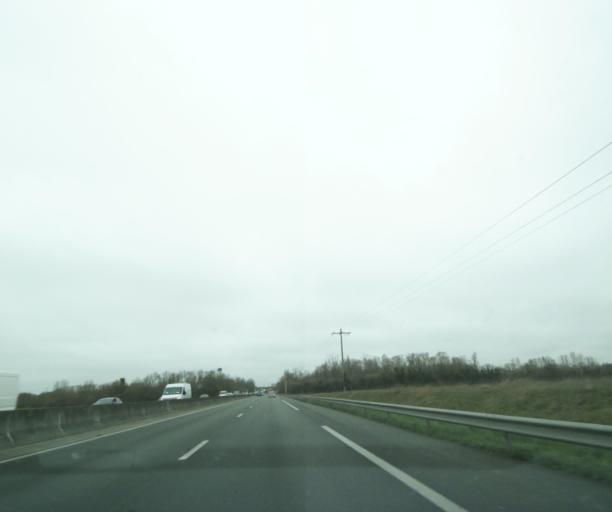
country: FR
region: Poitou-Charentes
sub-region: Departement de la Charente-Maritime
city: Aytre
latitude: 46.1464
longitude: -1.1094
